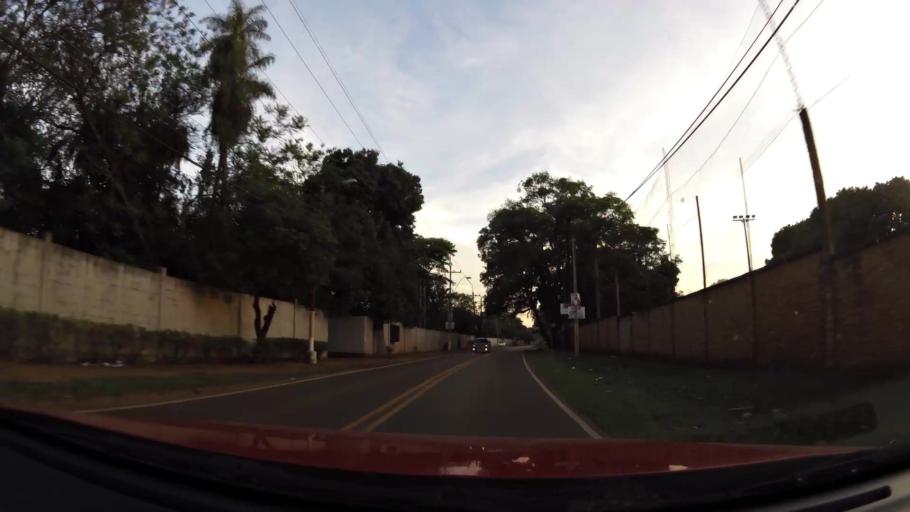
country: PY
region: Central
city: San Lorenzo
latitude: -25.3605
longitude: -57.4900
